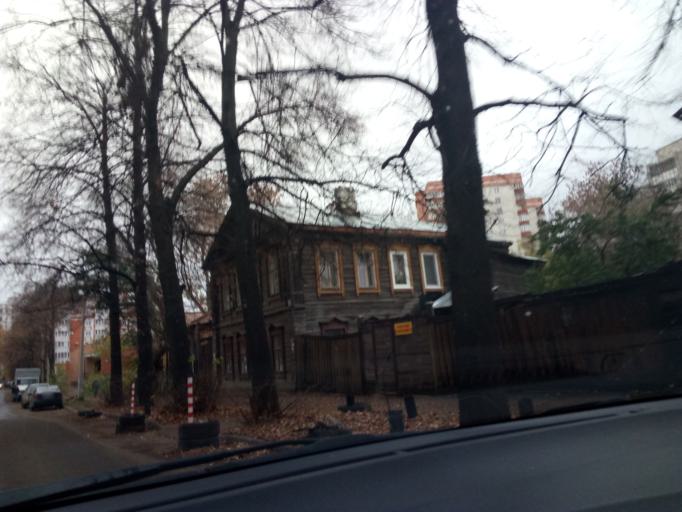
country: RU
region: Tatarstan
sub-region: Gorod Kazan'
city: Kazan
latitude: 55.7865
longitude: 49.1480
